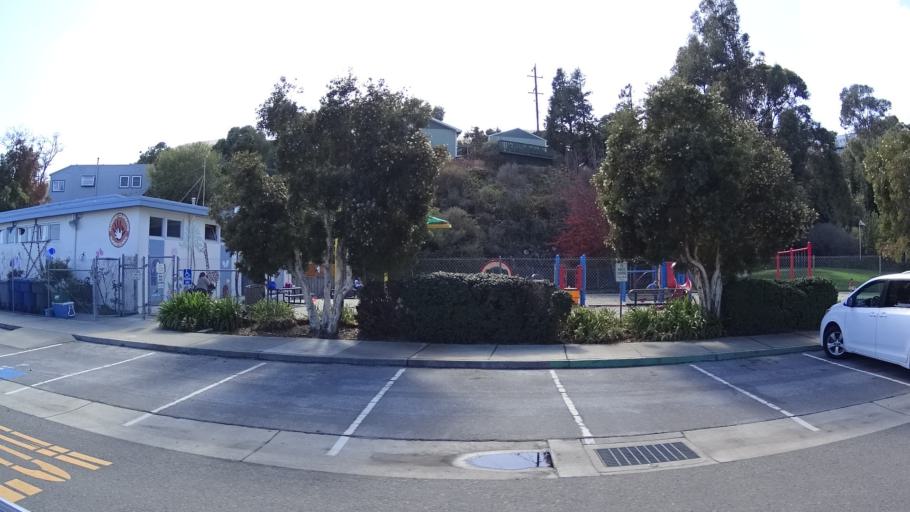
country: US
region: California
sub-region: San Mateo County
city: Brisbane
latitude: 37.6853
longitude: -122.4051
